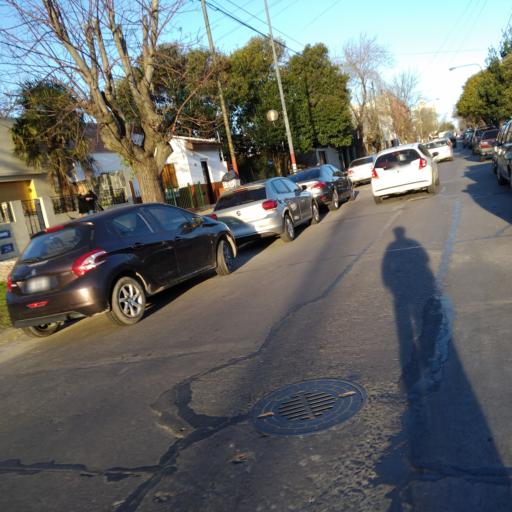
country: AR
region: Buenos Aires
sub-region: Partido de La Plata
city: La Plata
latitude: -34.9279
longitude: -57.9824
